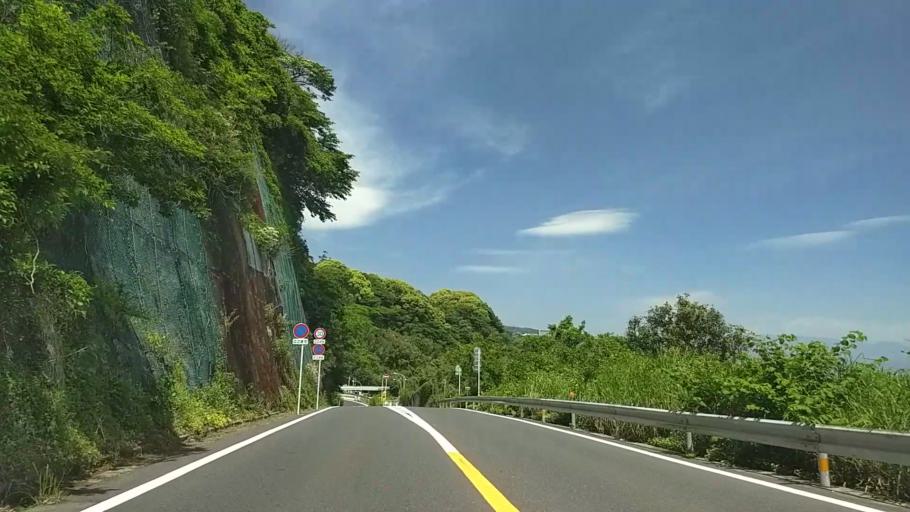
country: JP
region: Kanagawa
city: Yugawara
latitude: 35.1684
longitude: 139.1443
